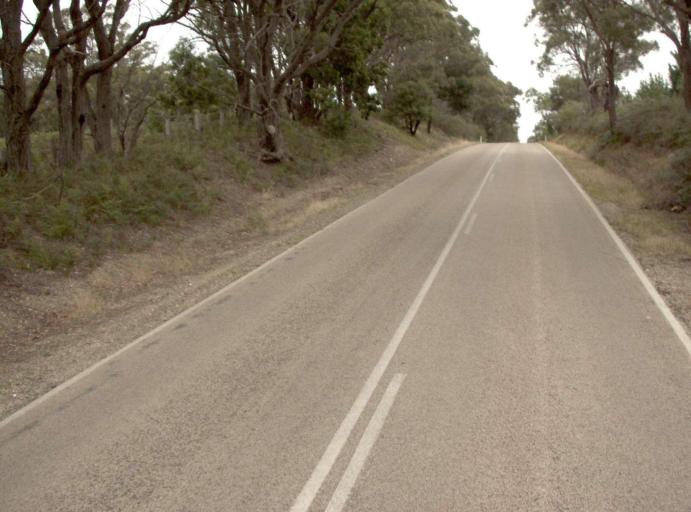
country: AU
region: Victoria
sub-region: East Gippsland
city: Bairnsdale
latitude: -37.8393
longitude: 147.4316
